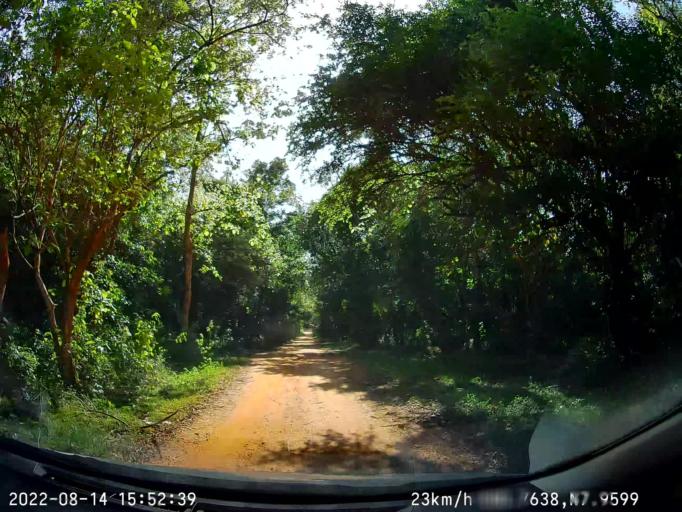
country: LK
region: Central
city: Sigiriya
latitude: 7.9600
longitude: 80.7635
